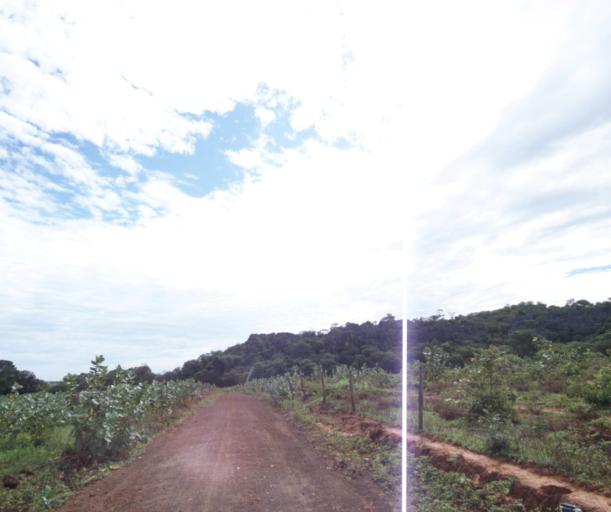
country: BR
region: Bahia
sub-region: Carinhanha
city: Carinhanha
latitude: -14.2431
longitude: -44.4156
